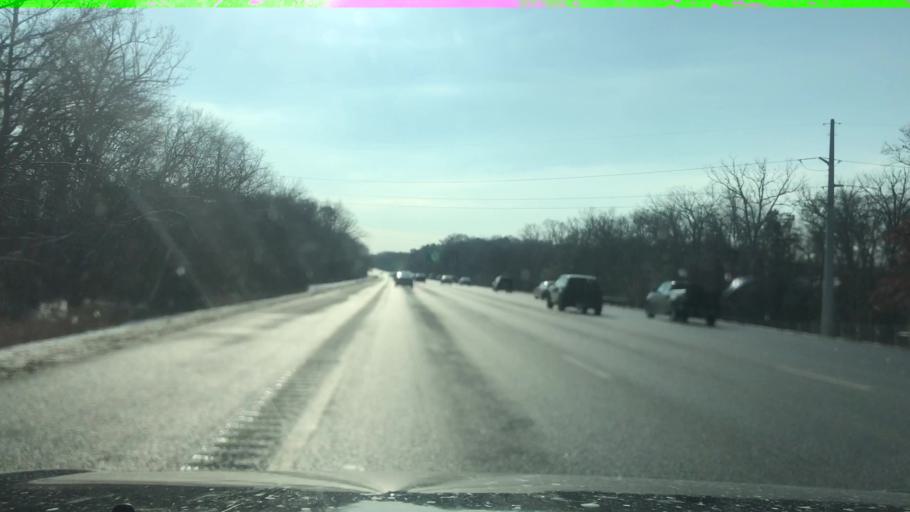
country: US
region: New Jersey
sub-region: Monmouth County
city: Shark River Hills
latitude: 40.1875
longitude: -74.1011
